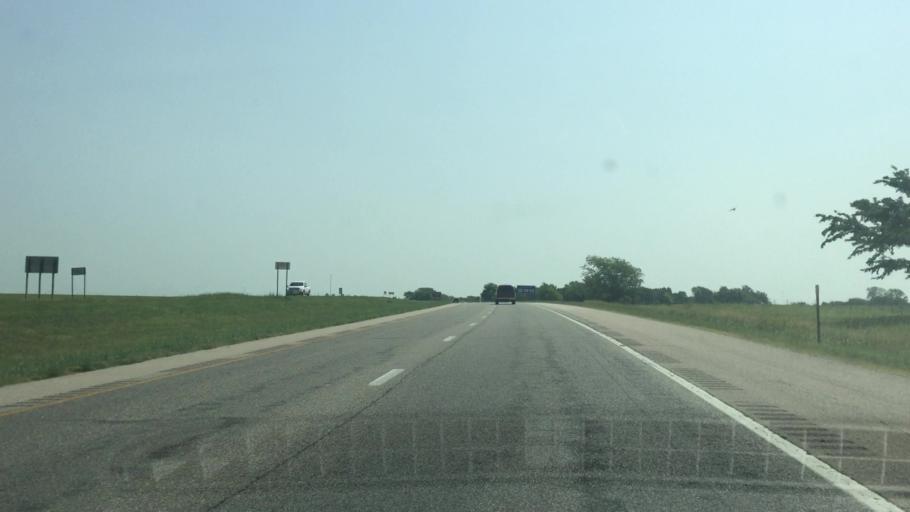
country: US
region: Kansas
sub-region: Osage County
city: Lyndon
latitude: 38.4259
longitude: -95.7438
